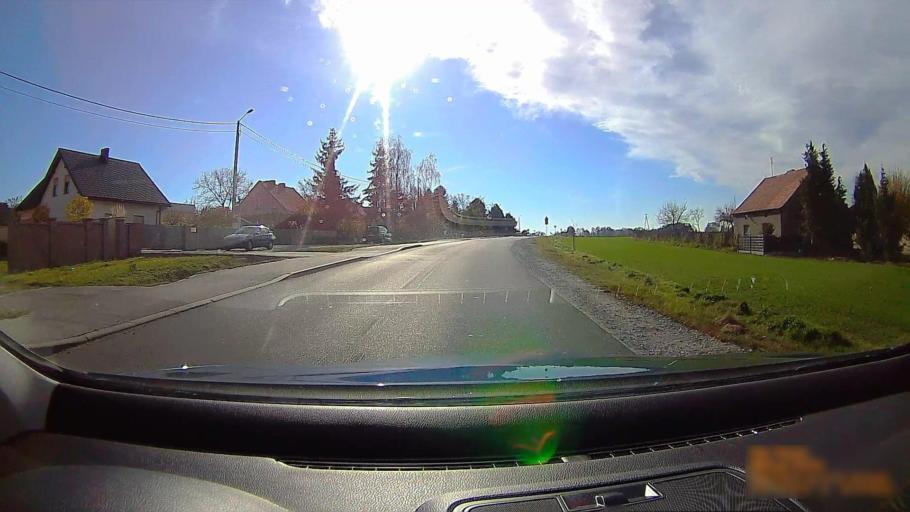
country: PL
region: Greater Poland Voivodeship
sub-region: Powiat ostrzeszowski
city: Doruchow
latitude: 51.3590
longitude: 18.0306
